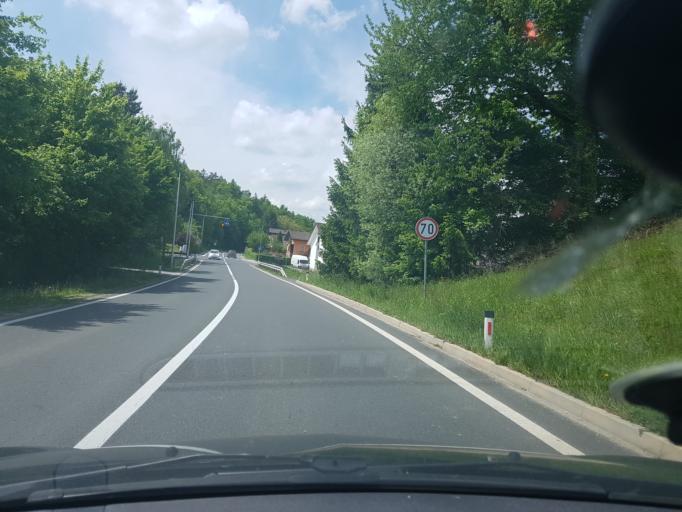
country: SI
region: Rogaska Slatina
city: Rogaska Slatina
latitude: 46.2518
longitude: 15.6308
